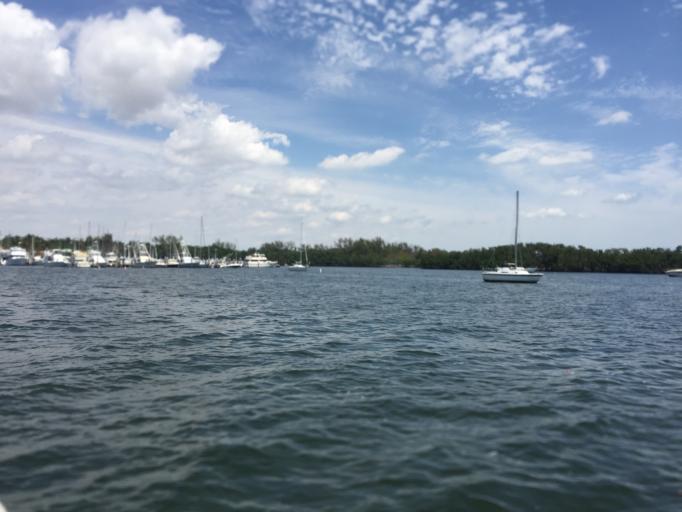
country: US
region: Florida
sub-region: Miami-Dade County
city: Coconut Grove
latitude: 25.7292
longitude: -80.2290
